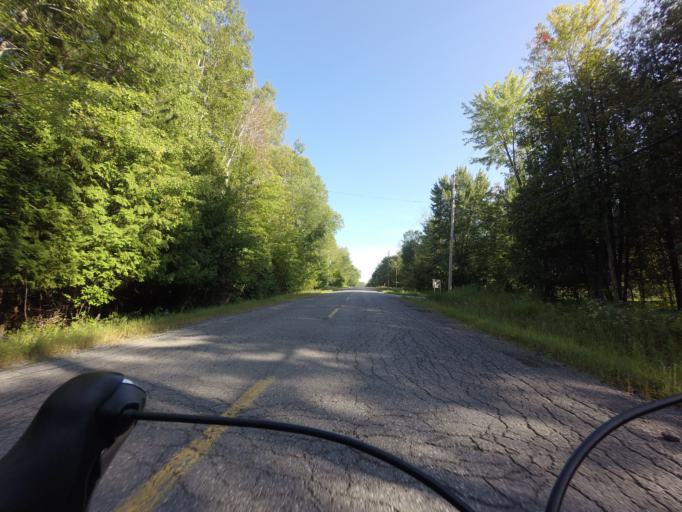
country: CA
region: Ontario
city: Bells Corners
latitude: 45.4724
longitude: -76.0348
